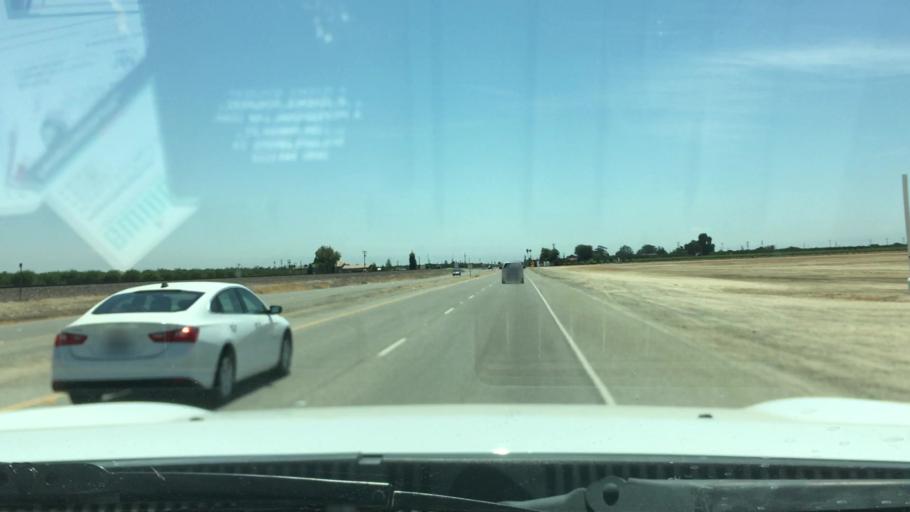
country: US
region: California
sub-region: Kern County
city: Shafter
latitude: 35.5239
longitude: -119.3000
